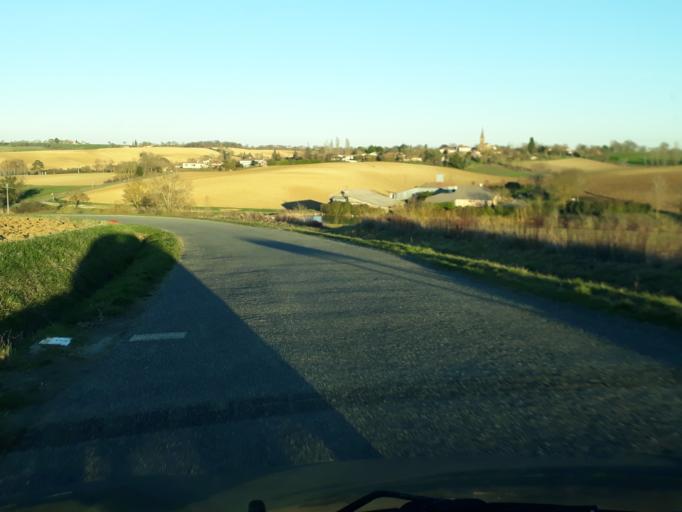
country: FR
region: Midi-Pyrenees
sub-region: Departement du Gers
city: Gimont
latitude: 43.6230
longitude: 0.9412
